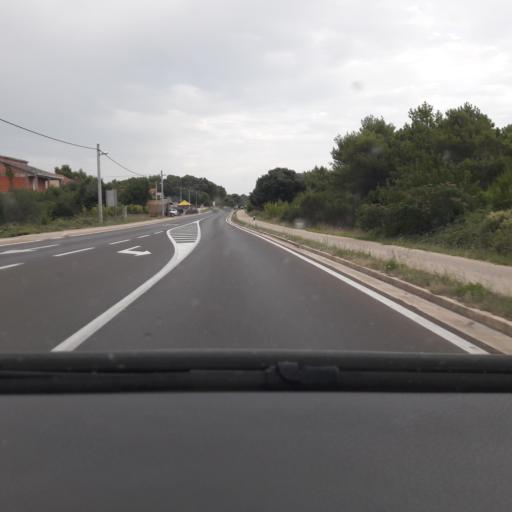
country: HR
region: Zadarska
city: Zadar
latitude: 44.1686
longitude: 15.1978
